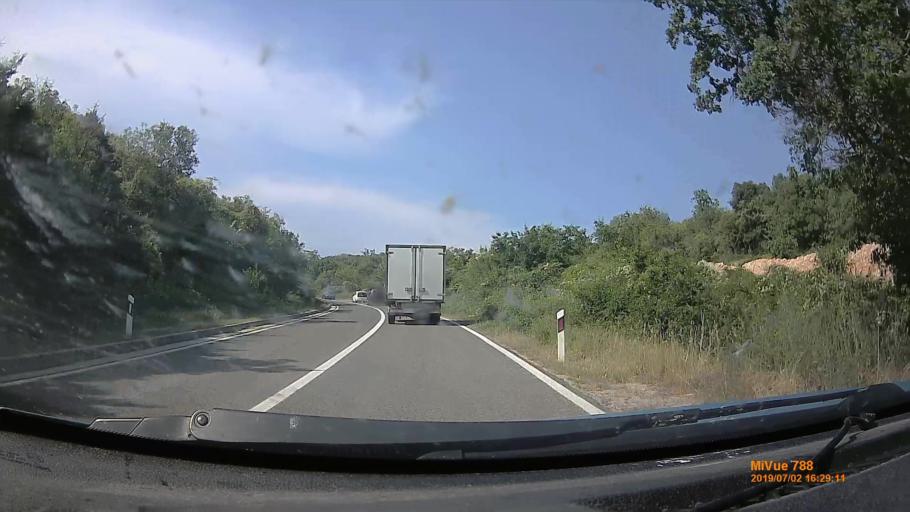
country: HR
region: Primorsko-Goranska
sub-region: Grad Krk
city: Krk
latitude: 45.0336
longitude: 14.4991
